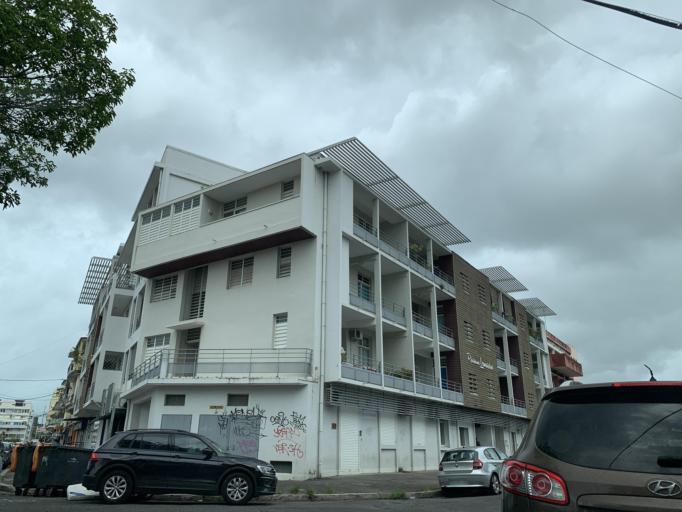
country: GP
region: Guadeloupe
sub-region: Guadeloupe
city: Pointe-a-Pitre
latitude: 16.2454
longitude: -61.5319
